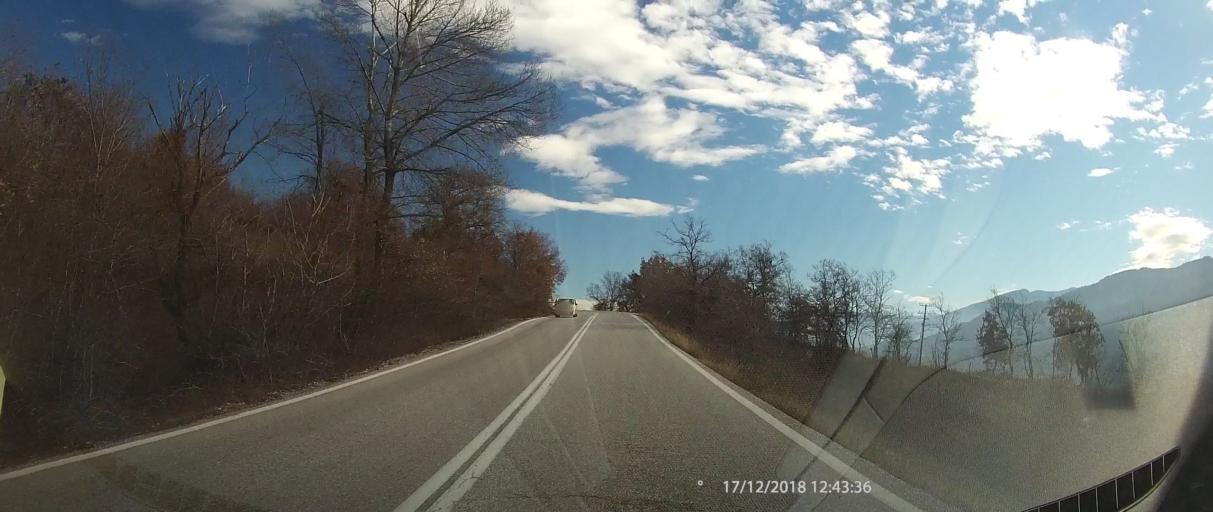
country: GR
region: Epirus
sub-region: Nomos Ioanninon
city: Metsovo
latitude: 39.7830
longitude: 21.3908
